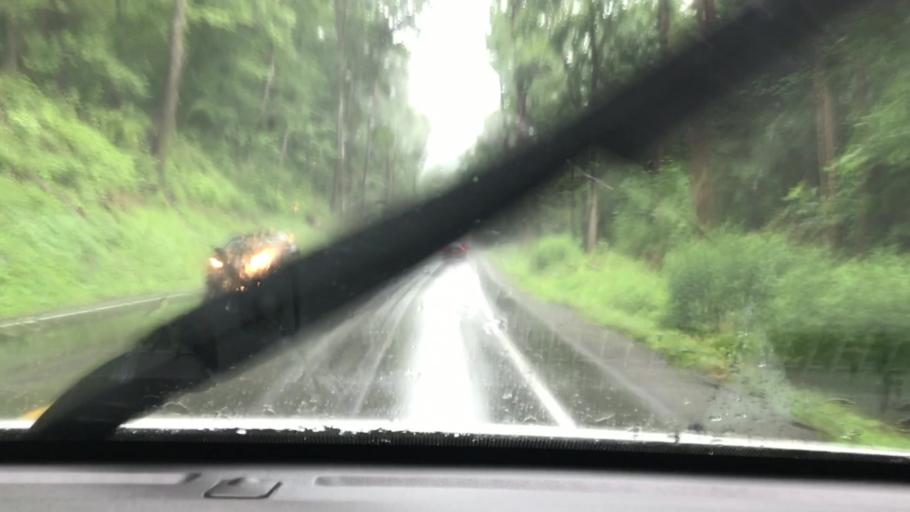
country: US
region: Pennsylvania
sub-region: Blair County
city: Tyrone
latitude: 40.7573
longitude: -78.2251
